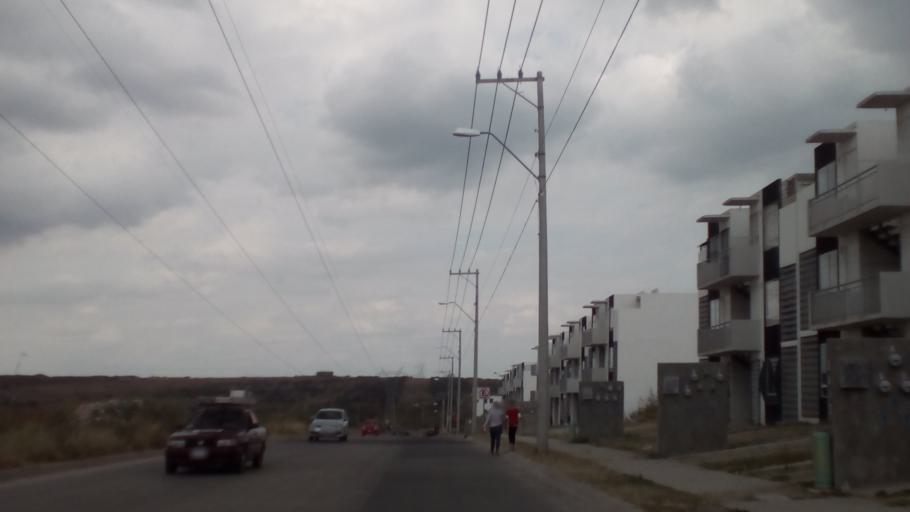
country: MX
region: Guanajuato
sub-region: Leon
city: Fraccionamiento Paseo de las Torres
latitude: 21.1758
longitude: -101.7651
